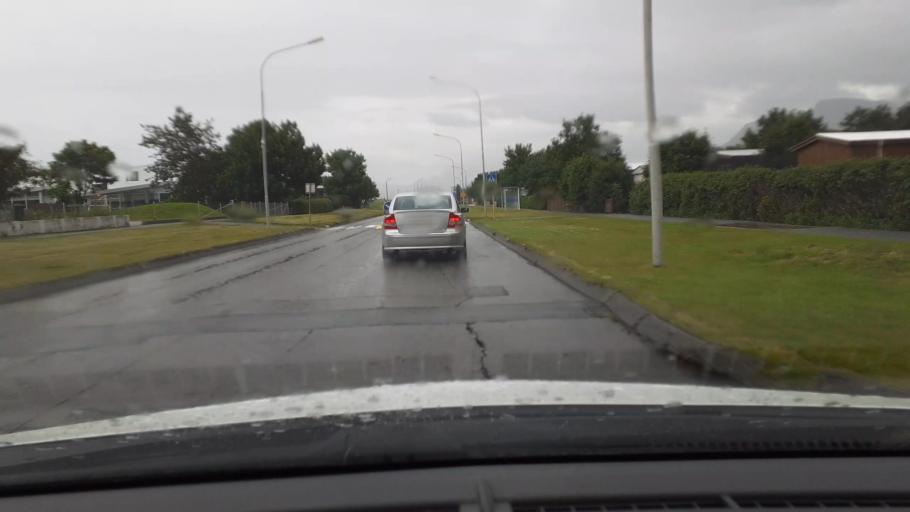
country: IS
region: West
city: Akranes
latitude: 64.3231
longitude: -22.0718
